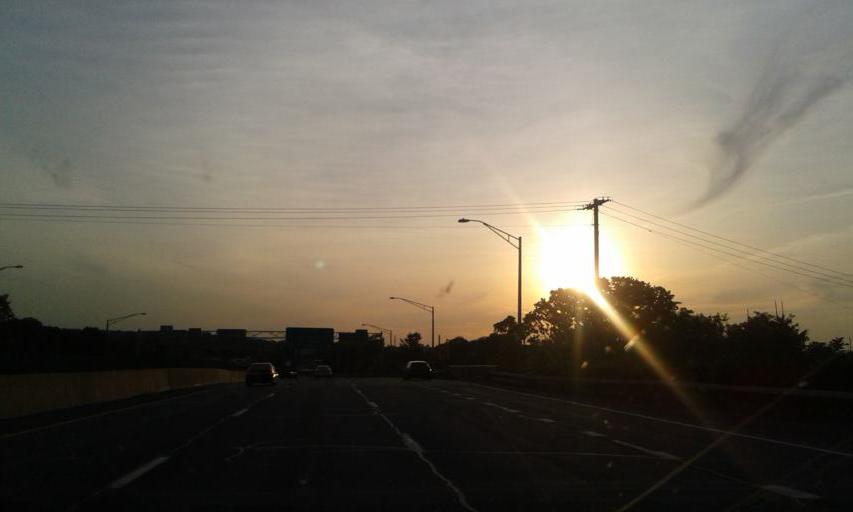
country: US
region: New York
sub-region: Onondaga County
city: Syracuse
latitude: 43.0557
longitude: -76.1650
